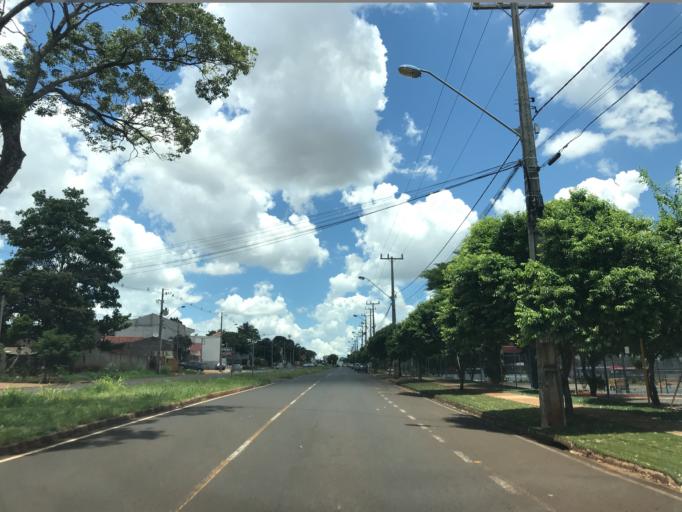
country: BR
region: Parana
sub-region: Maringa
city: Maringa
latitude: -23.3871
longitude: -51.9128
